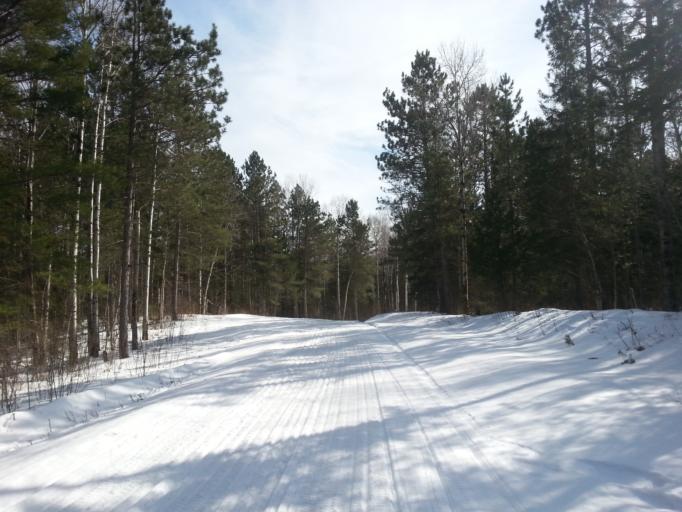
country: CA
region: Ontario
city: Greater Sudbury
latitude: 46.3401
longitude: -80.9022
